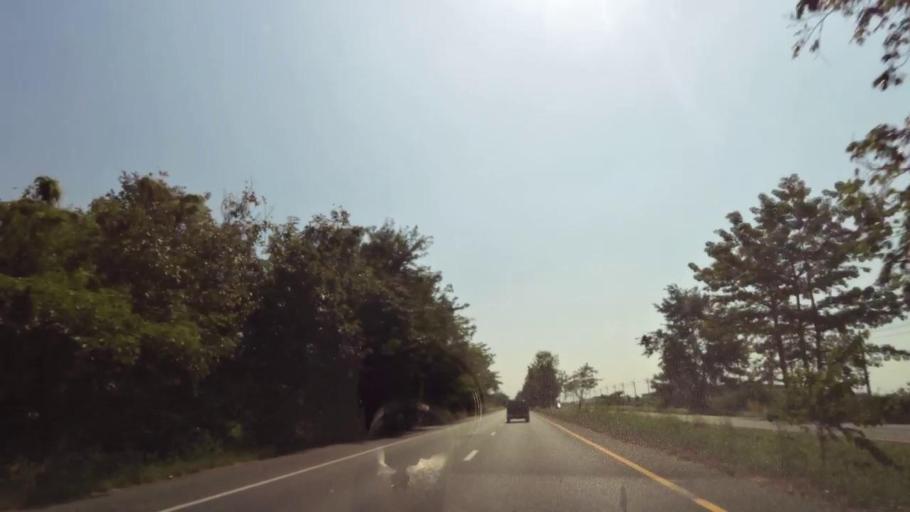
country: TH
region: Nakhon Sawan
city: Kao Liao
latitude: 15.9369
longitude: 100.1132
